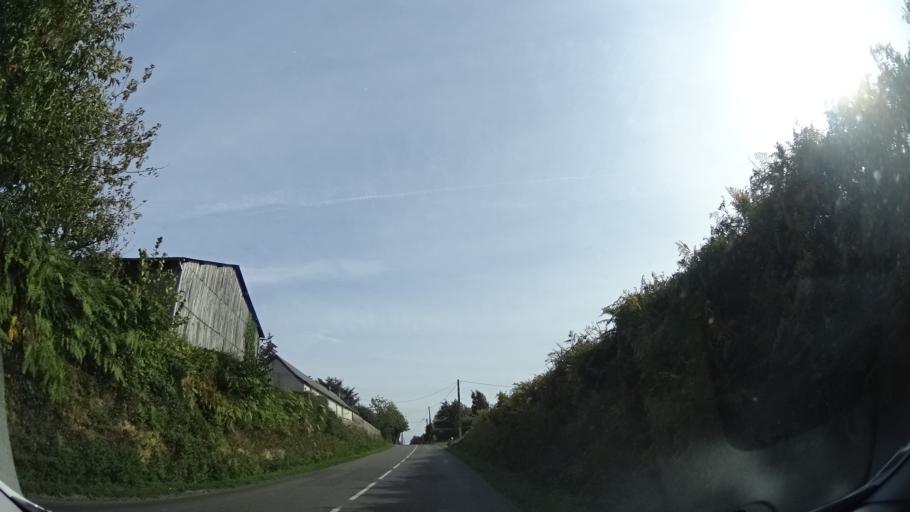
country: FR
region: Brittany
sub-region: Departement d'Ille-et-Vilaine
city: Melesse
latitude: 48.2163
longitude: -1.7101
